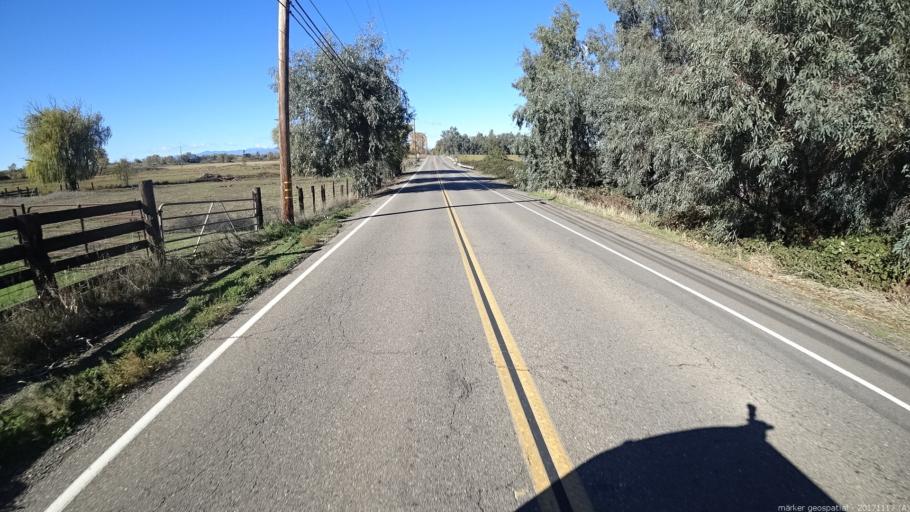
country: US
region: California
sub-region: Shasta County
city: Anderson
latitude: 40.4359
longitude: -122.2391
